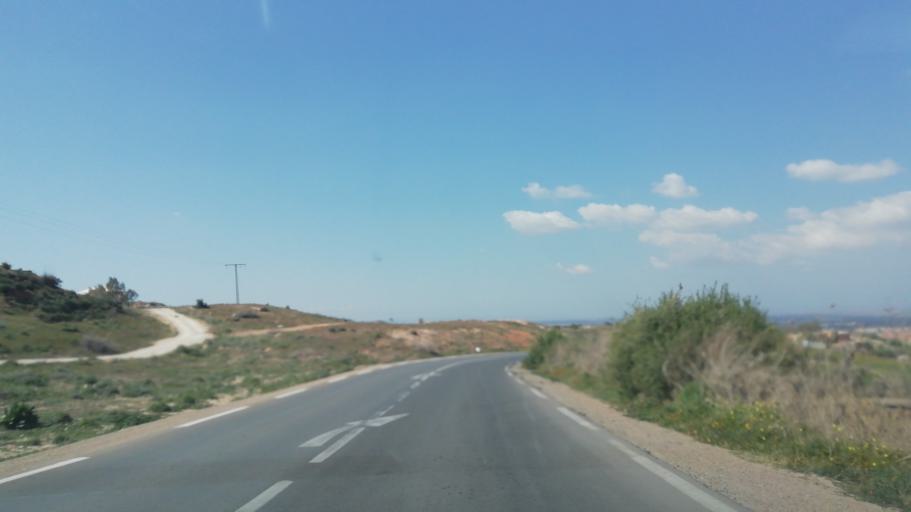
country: DZ
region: Mascara
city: Mascara
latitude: 35.5552
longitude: 0.0791
